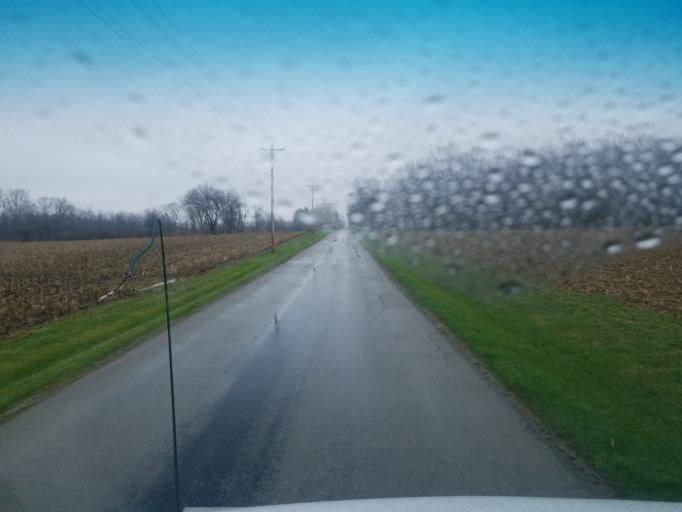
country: US
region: Ohio
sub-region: Seneca County
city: Tiffin
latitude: 40.9645
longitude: -83.1429
